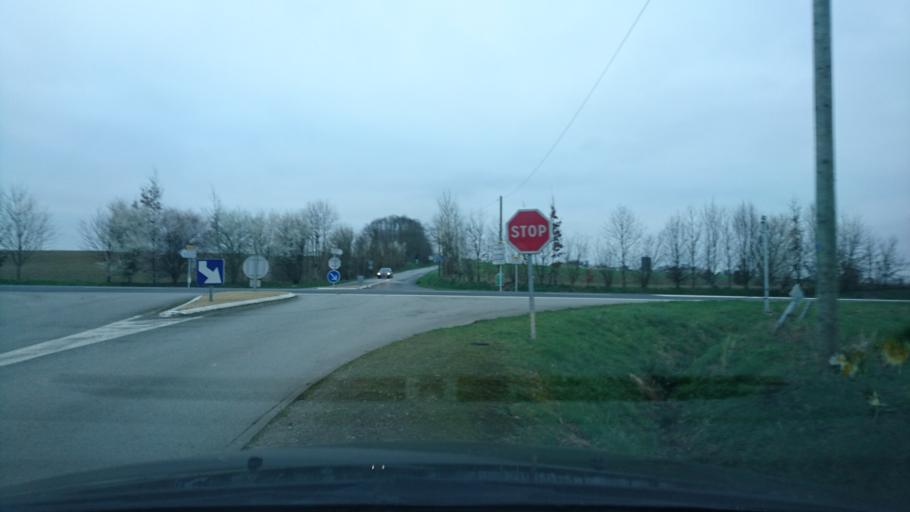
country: FR
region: Brittany
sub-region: Departement des Cotes-d'Armor
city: Plumieux
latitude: 48.0975
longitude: -2.5532
